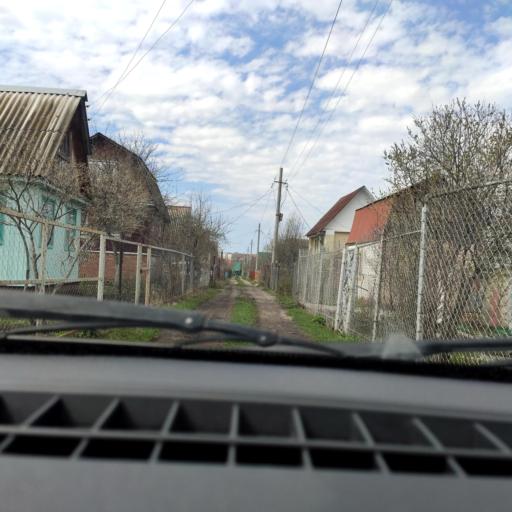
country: RU
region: Bashkortostan
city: Avdon
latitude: 54.7202
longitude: 55.7896
